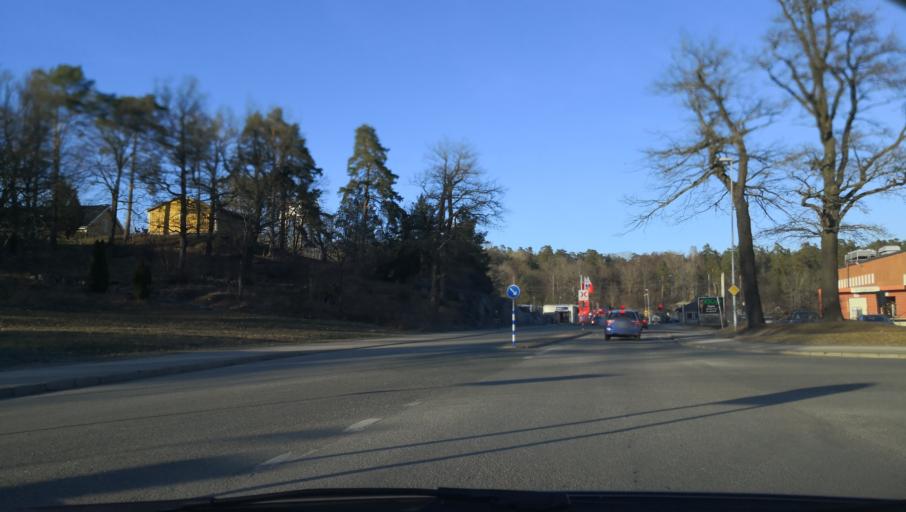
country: SE
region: Stockholm
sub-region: Varmdo Kommun
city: Gustavsberg
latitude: 59.3270
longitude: 18.3902
